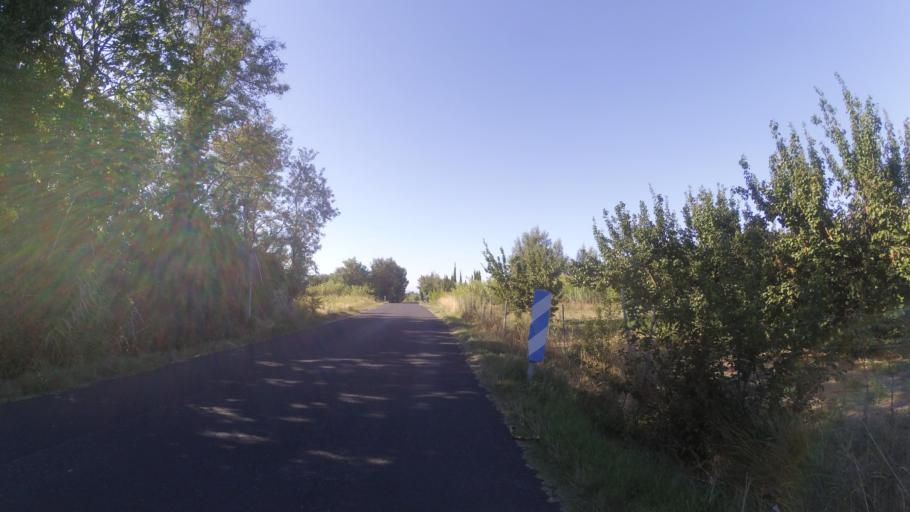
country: FR
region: Languedoc-Roussillon
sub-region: Departement des Pyrenees-Orientales
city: Villeneuve-la-Riviere
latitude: 42.7022
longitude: 2.7993
